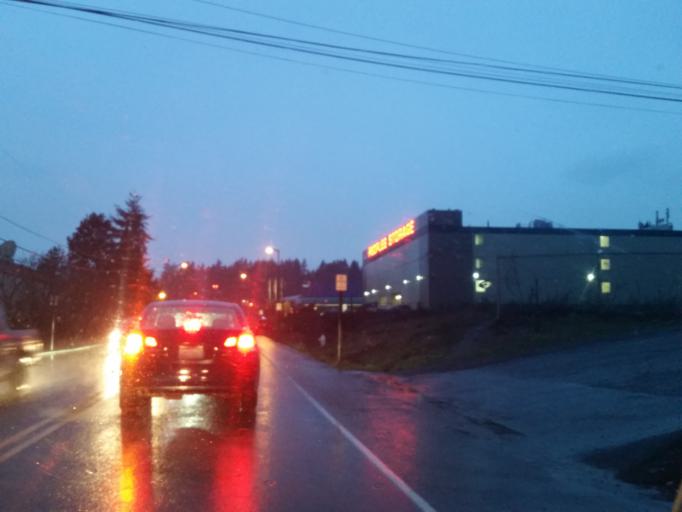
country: US
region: Washington
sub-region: King County
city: Kenmore
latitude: 47.7596
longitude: -122.2466
